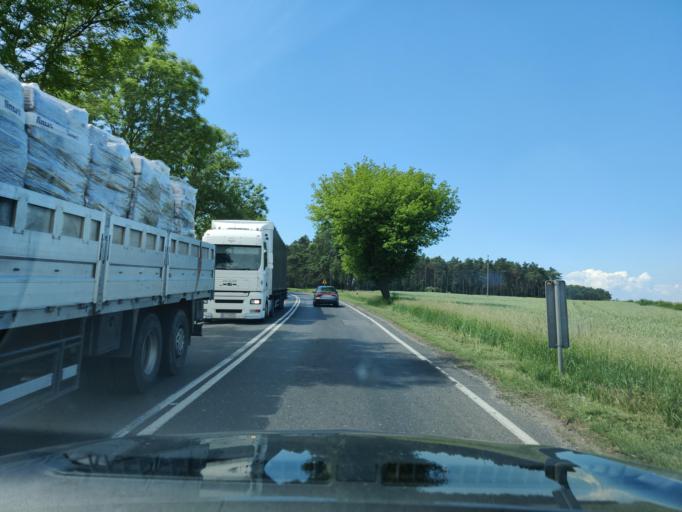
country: PL
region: Greater Poland Voivodeship
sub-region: Powiat grodziski
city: Rakoniewice
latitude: 52.1621
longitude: 16.3091
